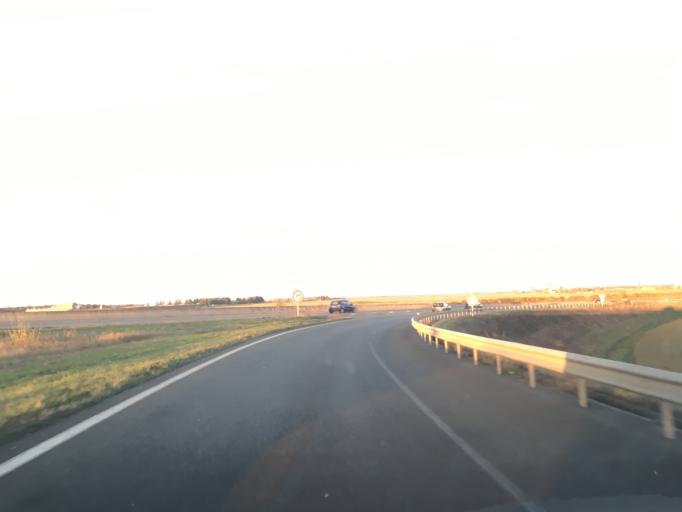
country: FR
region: Haute-Normandie
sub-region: Departement de l'Eure
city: Evreux
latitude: 49.0137
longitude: 1.1980
